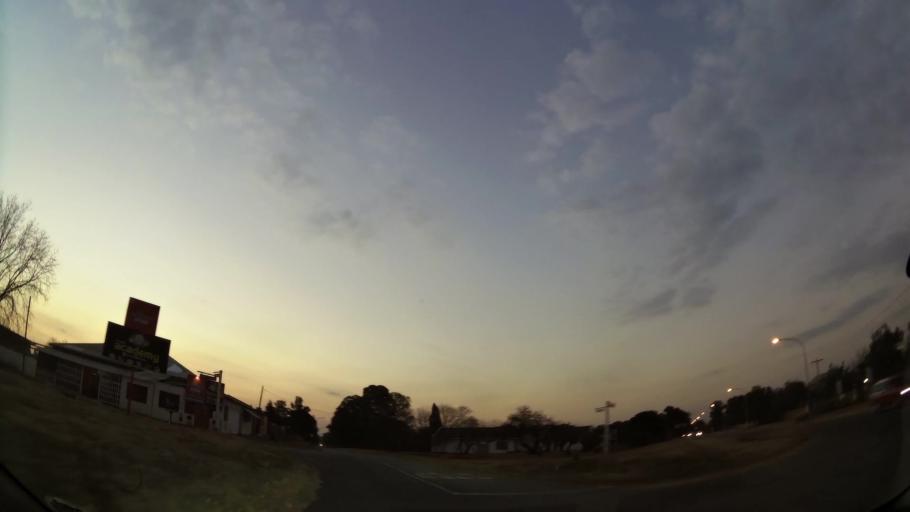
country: ZA
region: Gauteng
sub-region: Ekurhuleni Metropolitan Municipality
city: Benoni
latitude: -26.1354
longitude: 28.3146
